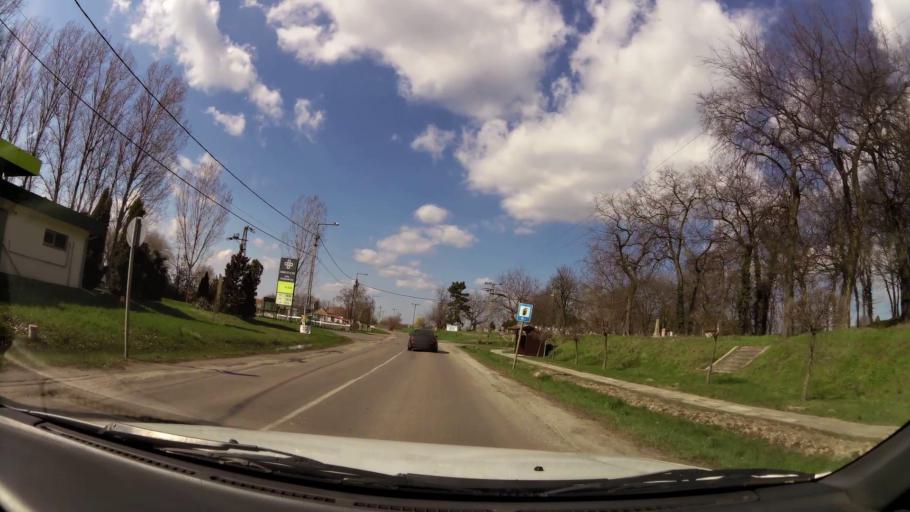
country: HU
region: Pest
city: Tapioszele
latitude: 47.3383
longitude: 19.8696
